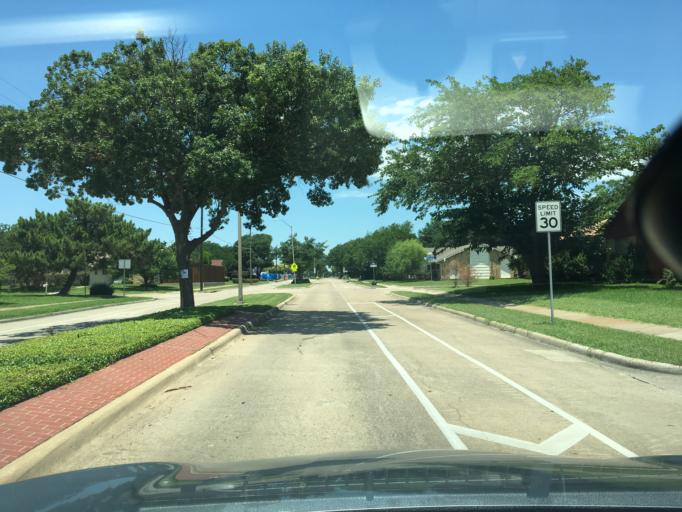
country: US
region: Texas
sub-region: Dallas County
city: Richardson
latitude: 32.9322
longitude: -96.6909
